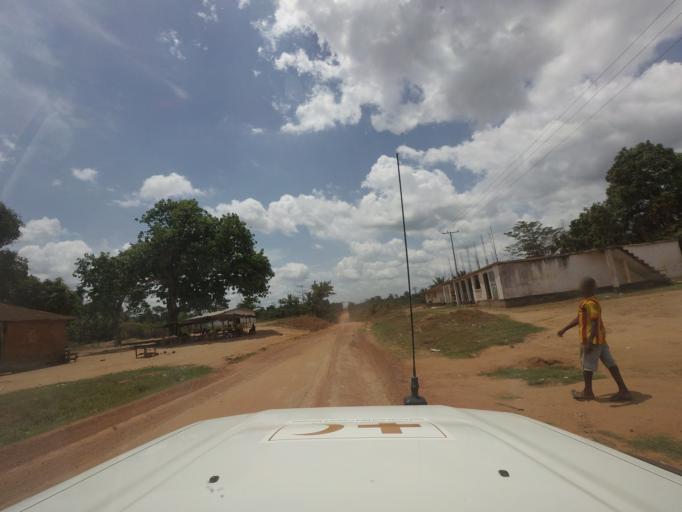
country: LR
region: Nimba
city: Sanniquellie
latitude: 7.2274
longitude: -8.9362
